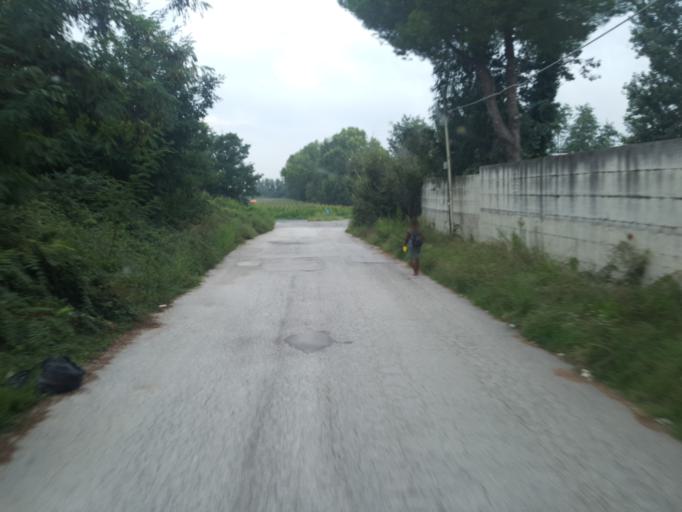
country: IT
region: Campania
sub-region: Provincia di Caserta
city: Pignataro Maggiore
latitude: 41.1682
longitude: 14.1543
